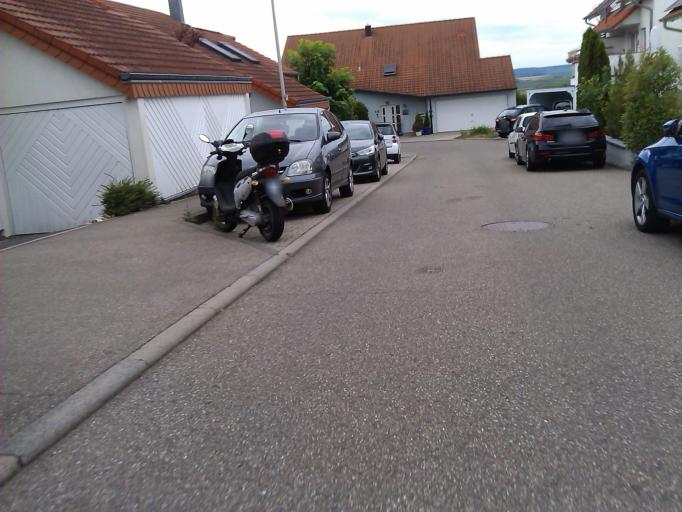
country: DE
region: Baden-Wuerttemberg
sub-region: Regierungsbezirk Stuttgart
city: Talheim
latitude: 49.0777
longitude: 9.1917
